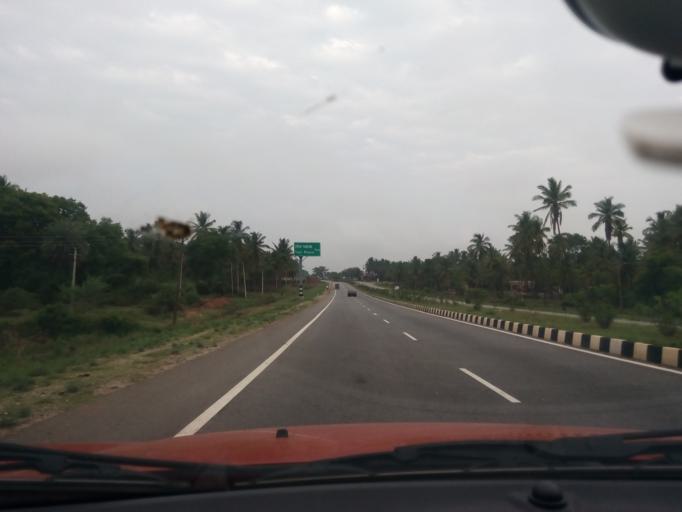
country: IN
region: Karnataka
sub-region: Mandya
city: Belluru
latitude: 12.9616
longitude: 76.6329
